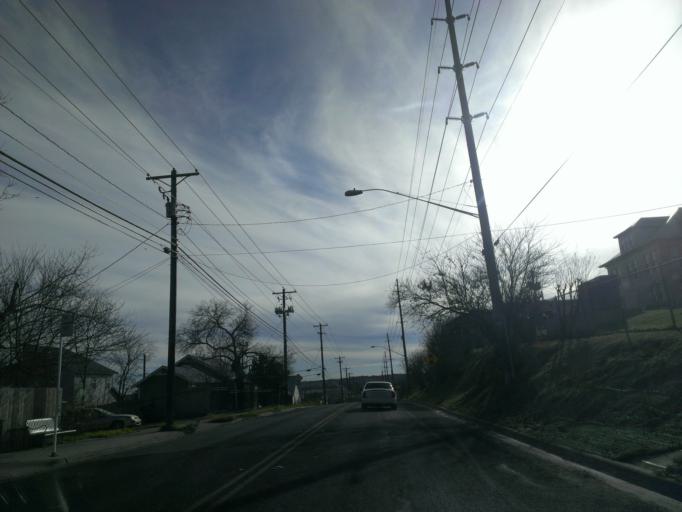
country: US
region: Texas
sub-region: Travis County
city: Austin
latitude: 30.2643
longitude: -97.7214
